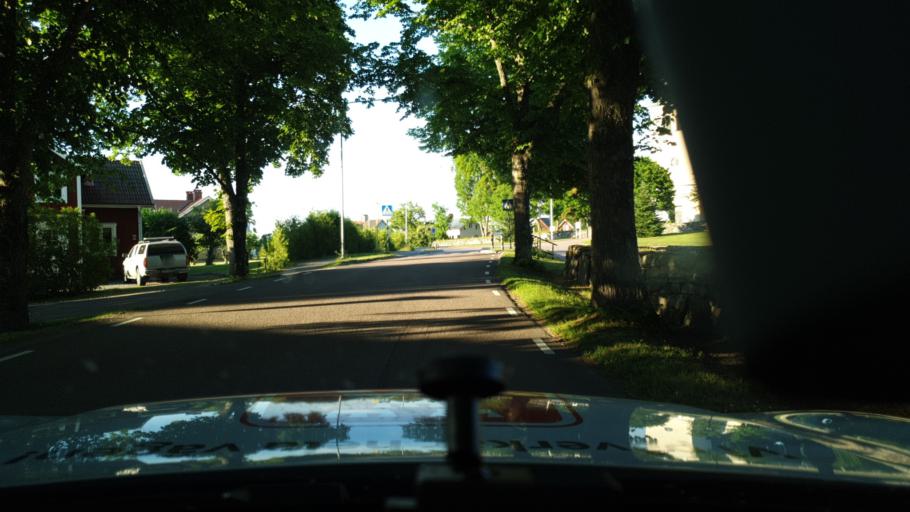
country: SE
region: Vaermland
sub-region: Kils Kommun
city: Kil
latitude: 59.5274
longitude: 13.3136
